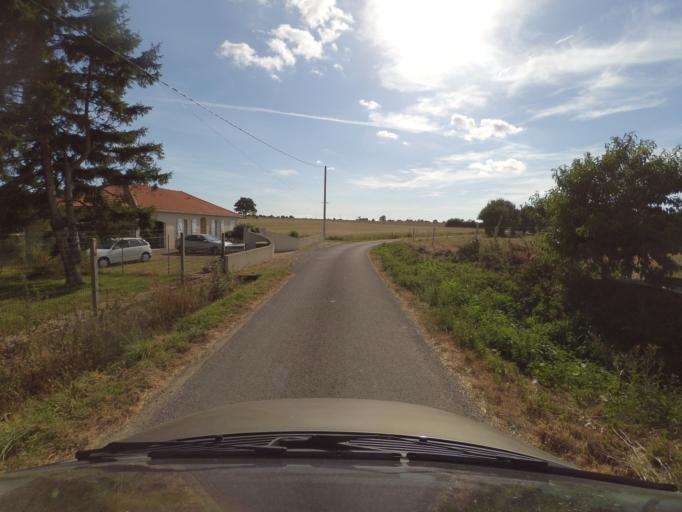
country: FR
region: Pays de la Loire
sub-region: Departement de la Loire-Atlantique
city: Montbert
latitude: 47.0509
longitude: -1.4866
